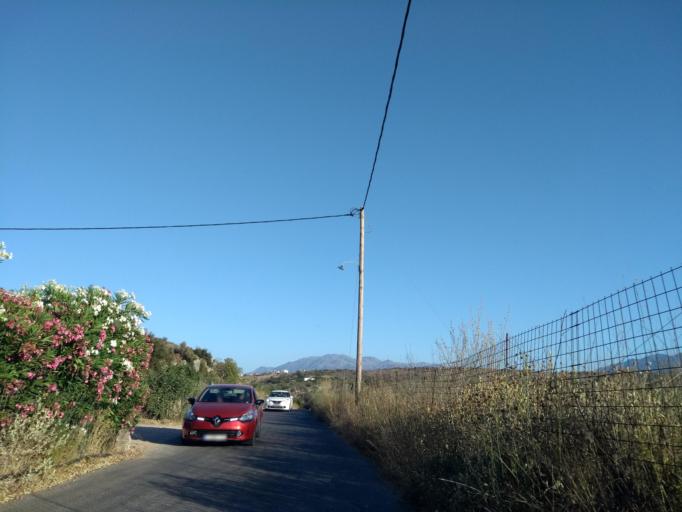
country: GR
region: Crete
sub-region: Nomos Chanias
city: Kalivai
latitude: 35.4311
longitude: 24.1766
